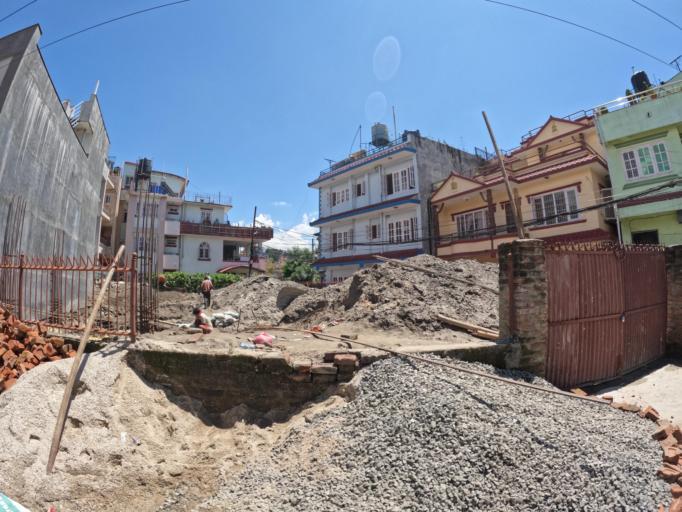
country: NP
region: Central Region
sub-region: Bagmati Zone
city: Kathmandu
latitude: 27.7480
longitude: 85.3251
